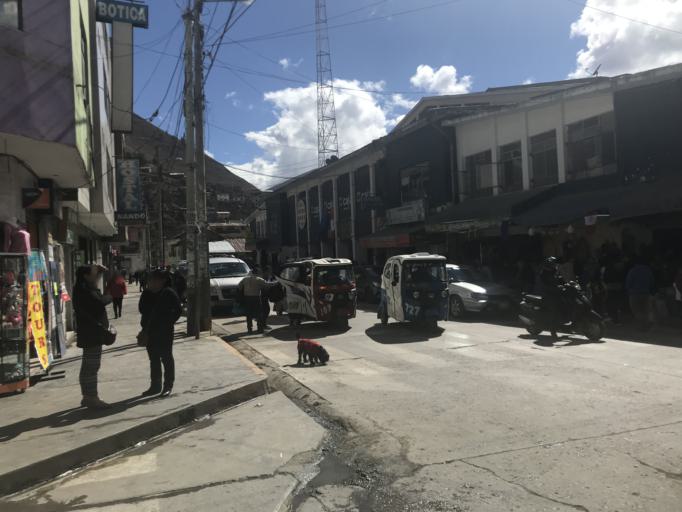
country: PE
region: Junin
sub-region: Provincia de Tarma
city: Tarma
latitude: -11.4183
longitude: -75.6881
